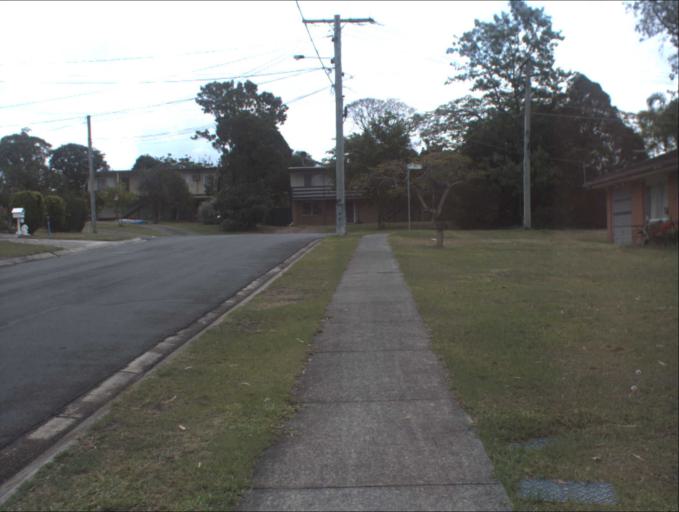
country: AU
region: Queensland
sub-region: Logan
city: Logan City
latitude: -27.6472
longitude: 153.1166
